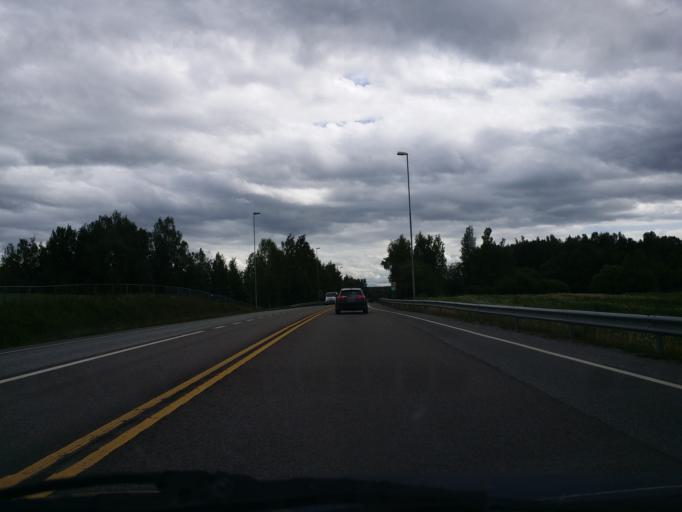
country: NO
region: Hedmark
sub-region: Hamar
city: Hamar
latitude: 60.7988
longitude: 11.1189
